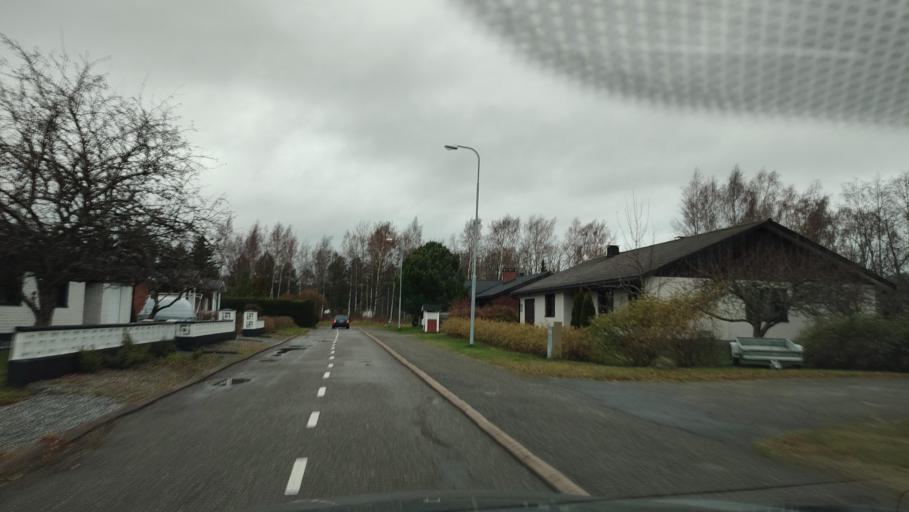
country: FI
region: Ostrobothnia
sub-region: Sydosterbotten
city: Kristinestad
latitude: 62.2800
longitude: 21.3648
